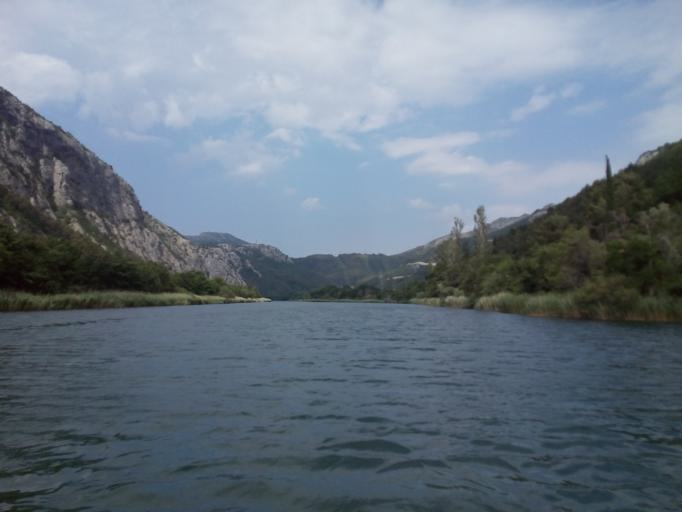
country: HR
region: Splitsko-Dalmatinska
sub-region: Grad Omis
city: Omis
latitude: 43.4488
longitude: 16.7192
